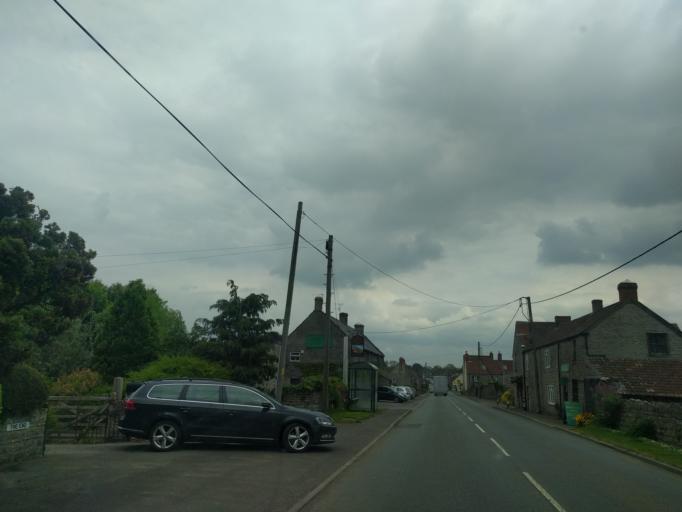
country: GB
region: England
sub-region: Somerset
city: Ilchester
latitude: 51.0763
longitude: -2.6486
